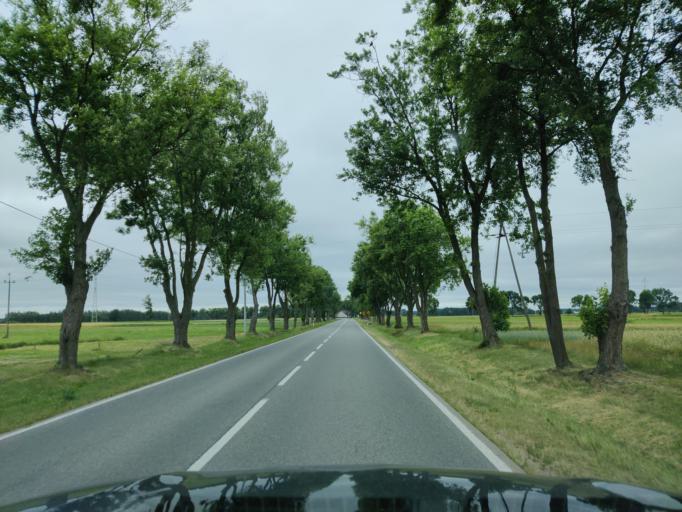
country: PL
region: Masovian Voivodeship
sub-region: Powiat ostrolecki
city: Czarnia
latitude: 53.3247
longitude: 21.1463
